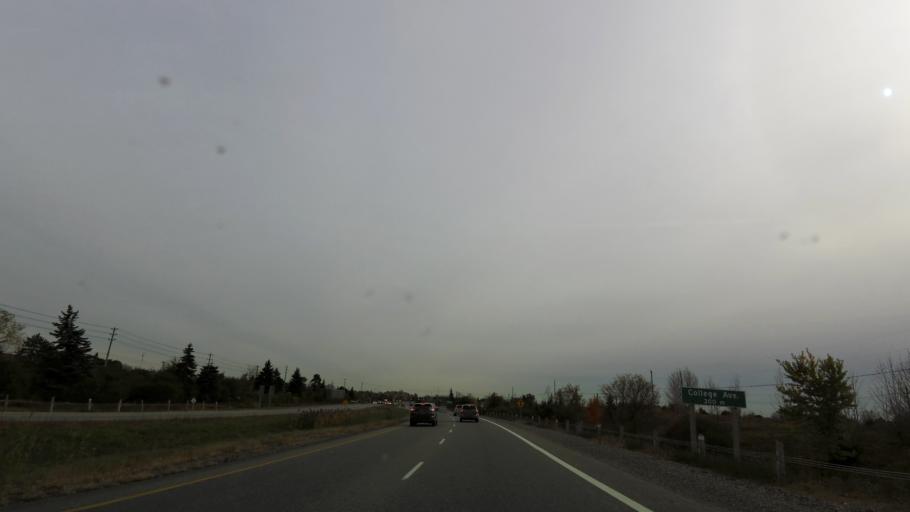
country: CA
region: Ontario
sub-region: Wellington County
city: Guelph
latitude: 43.5216
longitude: -80.2533
